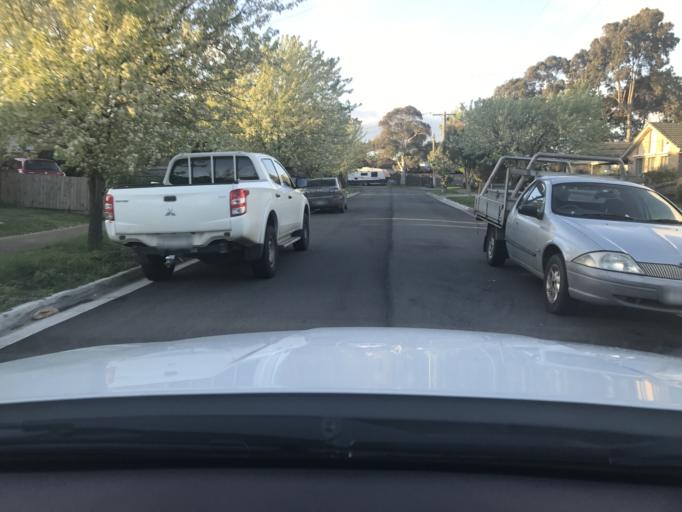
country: AU
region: Victoria
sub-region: Hume
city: Craigieburn
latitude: -37.5948
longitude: 144.9326
